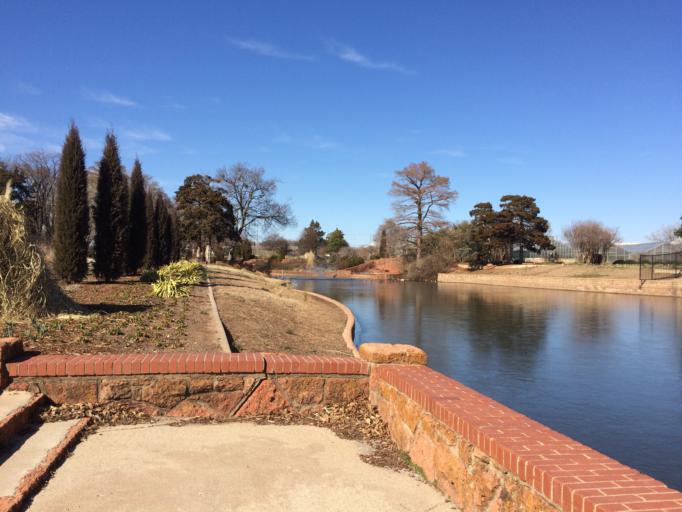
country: US
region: Oklahoma
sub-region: Oklahoma County
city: Warr Acres
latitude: 35.5056
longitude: -97.5785
